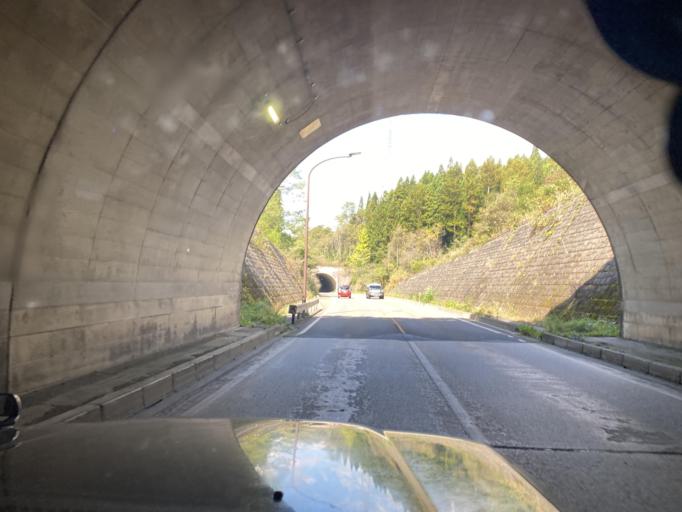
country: JP
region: Nagano
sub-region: Kitaazumi Gun
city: Hakuba
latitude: 36.6164
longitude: 137.8620
